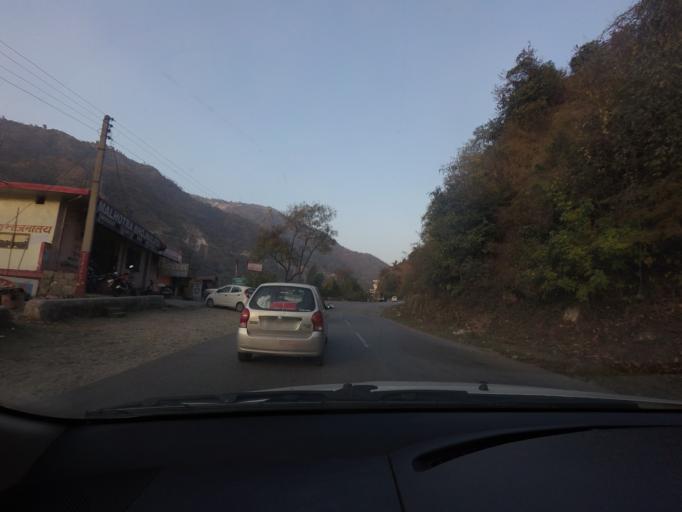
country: IN
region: Himachal Pradesh
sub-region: Mandi
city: Mandi
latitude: 31.7039
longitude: 76.9776
